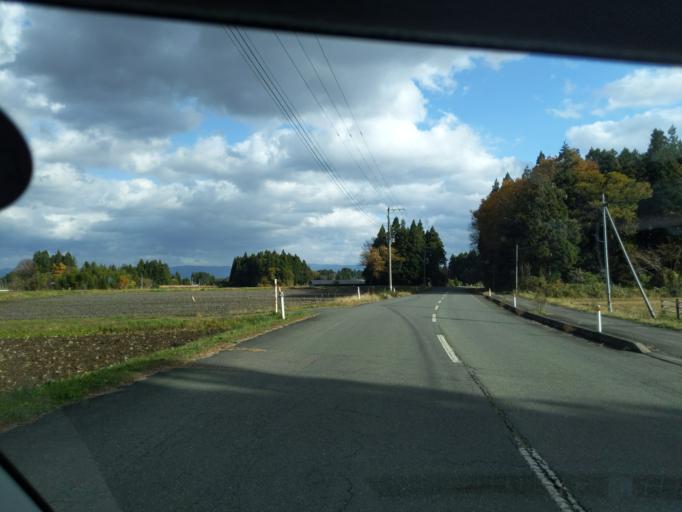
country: JP
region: Iwate
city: Mizusawa
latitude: 39.1139
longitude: 141.0159
